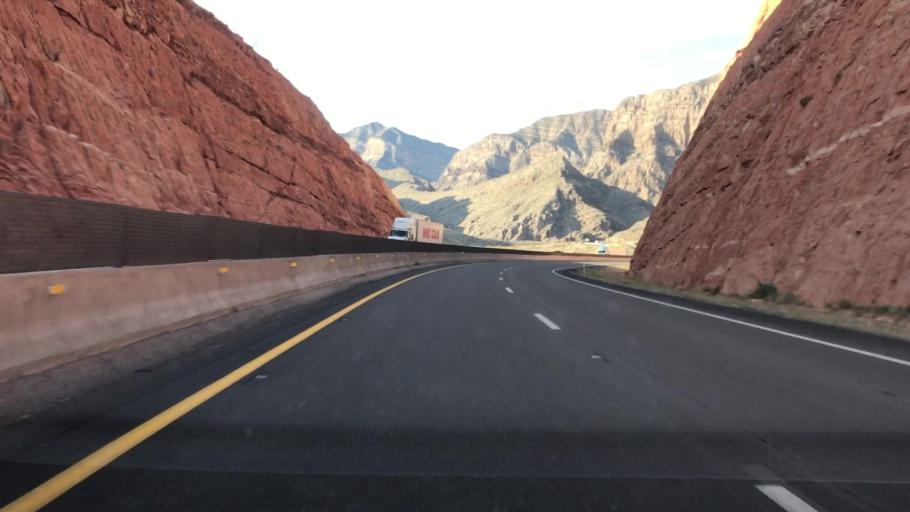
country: US
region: Arizona
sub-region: Mohave County
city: Beaver Dam
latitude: 36.9476
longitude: -113.8049
